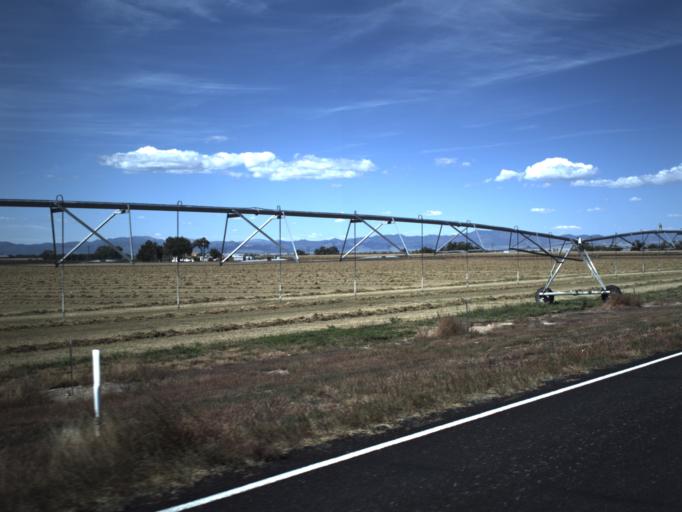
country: US
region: Utah
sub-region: Washington County
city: Enterprise
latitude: 37.6966
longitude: -113.6565
